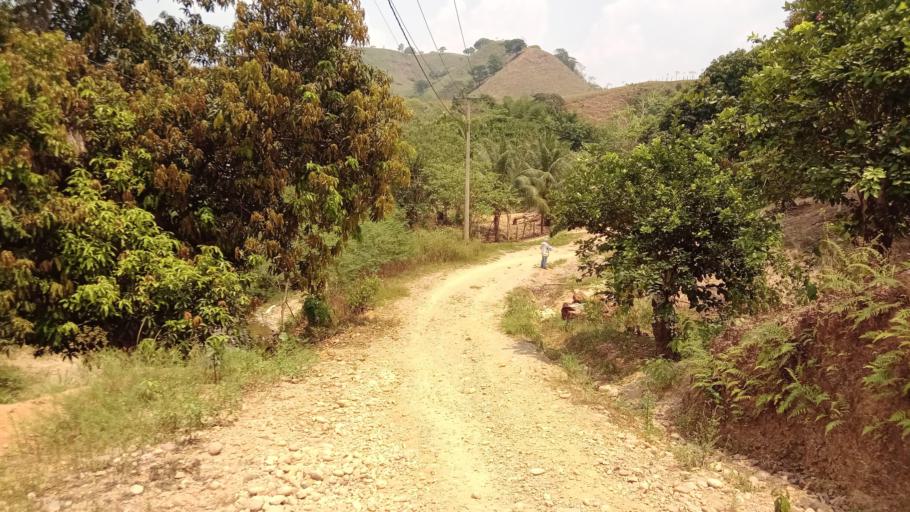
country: MX
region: Tabasco
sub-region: Huimanguillo
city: Francisco Rueda
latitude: 17.5897
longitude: -93.8572
